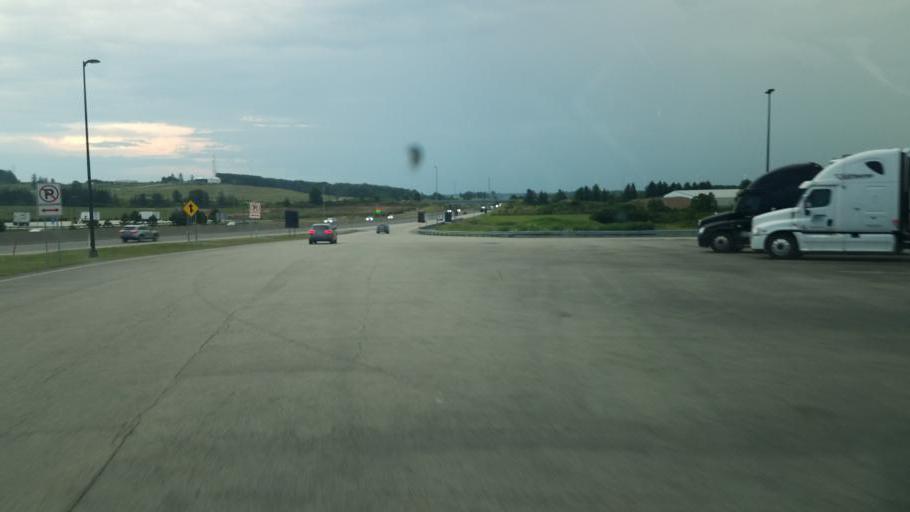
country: US
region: Pennsylvania
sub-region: Somerset County
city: Somerset
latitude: 39.9993
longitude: -79.0449
